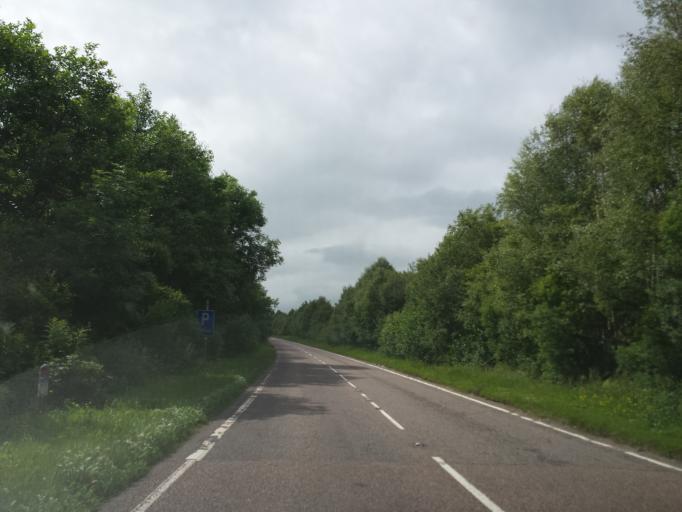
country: GB
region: Scotland
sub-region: Highland
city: Fort William
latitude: 56.8563
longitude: -5.2915
